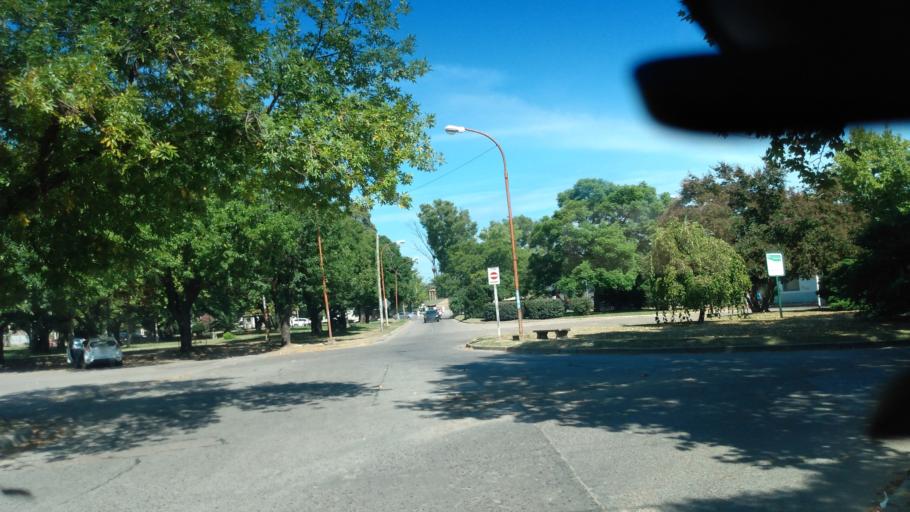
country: AR
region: Buenos Aires
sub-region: Partido de Lujan
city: Lujan
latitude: -34.5771
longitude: -59.1056
